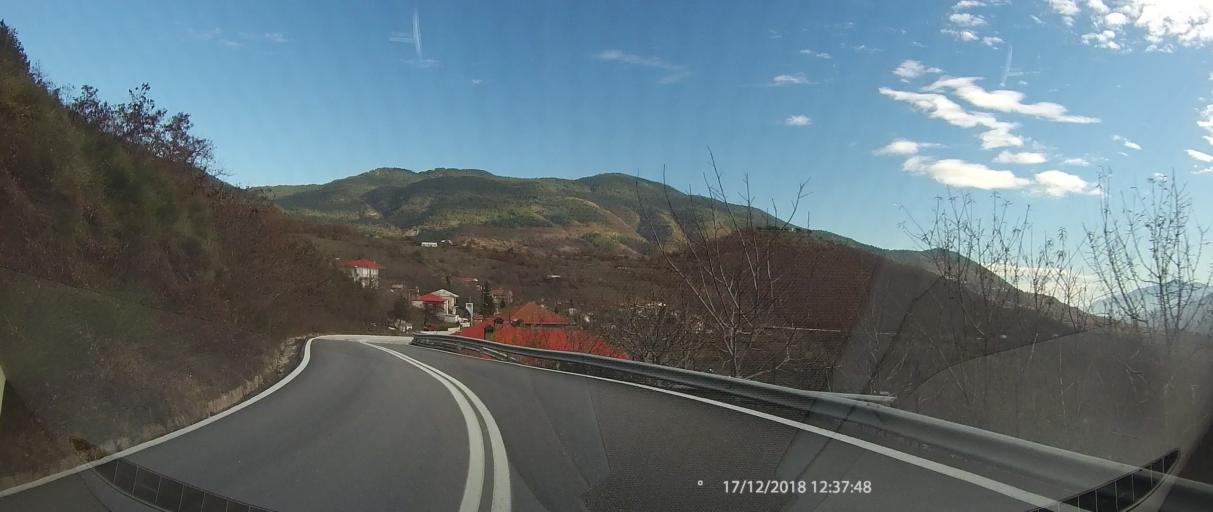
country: GR
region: Epirus
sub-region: Nomos Ioanninon
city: Metsovo
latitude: 39.8088
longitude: 21.3405
